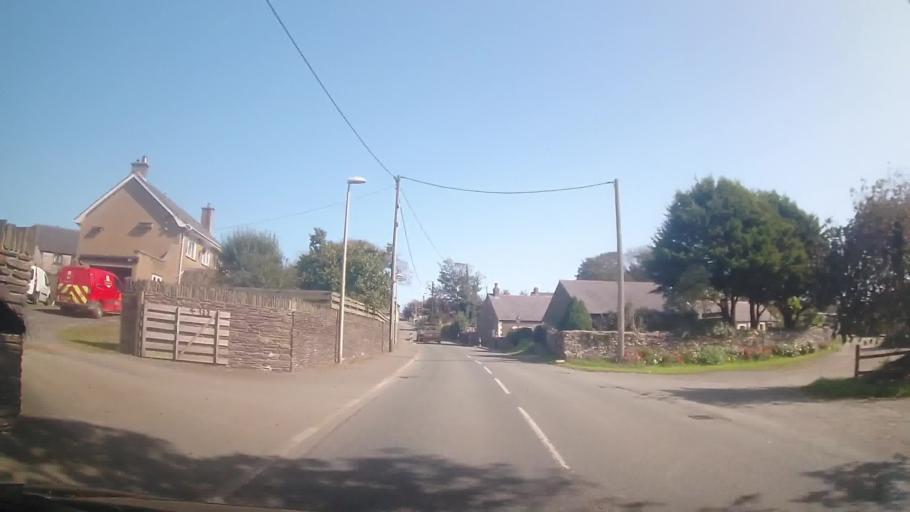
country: GB
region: Wales
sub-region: Pembrokeshire
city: Scleddau
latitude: 51.9268
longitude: -5.0035
